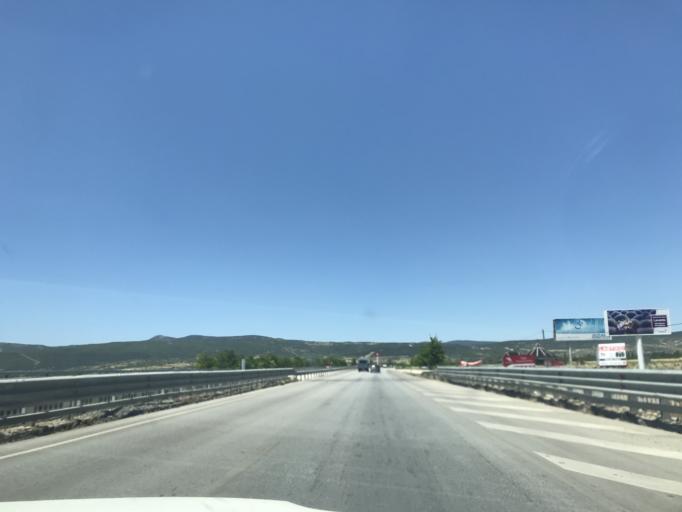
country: TR
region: Isparta
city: Keciborlu
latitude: 37.8991
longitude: 30.3461
